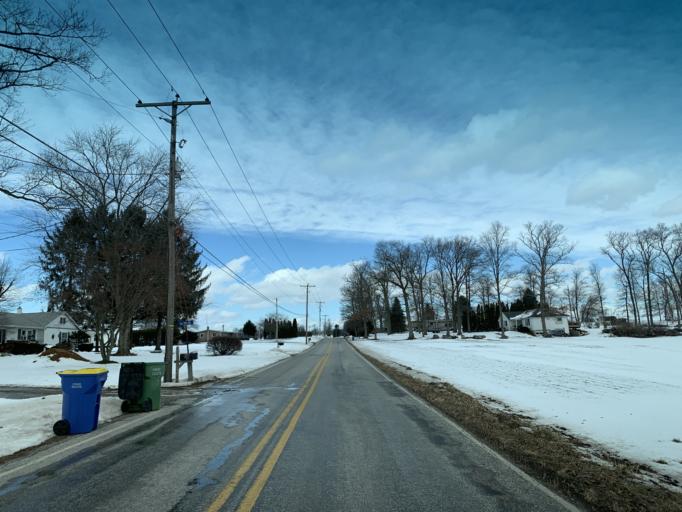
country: US
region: Pennsylvania
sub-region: York County
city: Stewartstown
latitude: 39.7649
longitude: -76.6336
